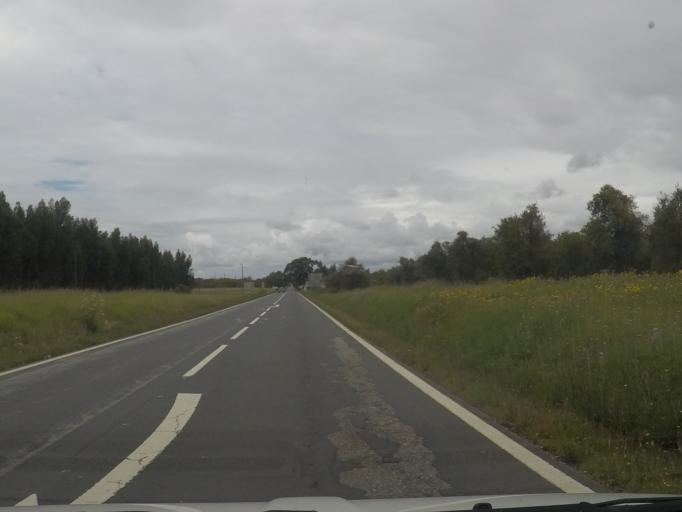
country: PT
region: Setubal
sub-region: Santiago do Cacem
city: Cercal
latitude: 37.8486
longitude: -8.7089
